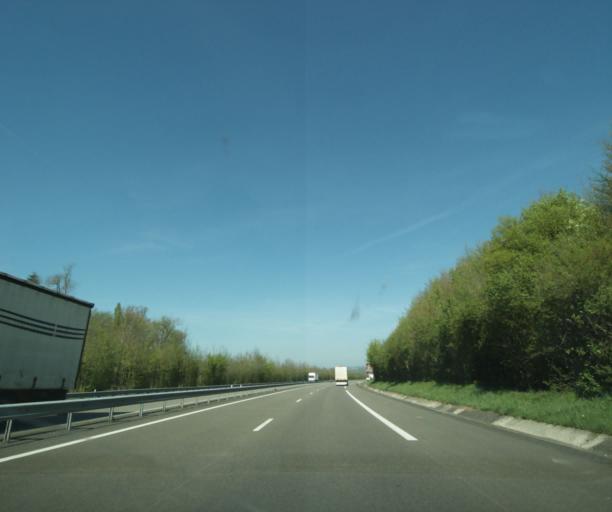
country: FR
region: Bourgogne
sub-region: Departement de la Nievre
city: Challuy
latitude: 46.9318
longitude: 3.1577
